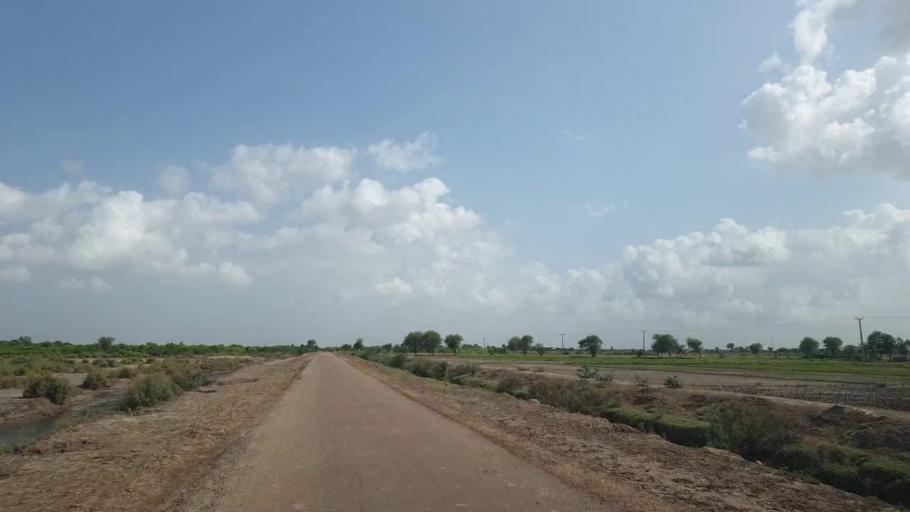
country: PK
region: Sindh
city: Kadhan
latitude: 24.5658
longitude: 69.0676
